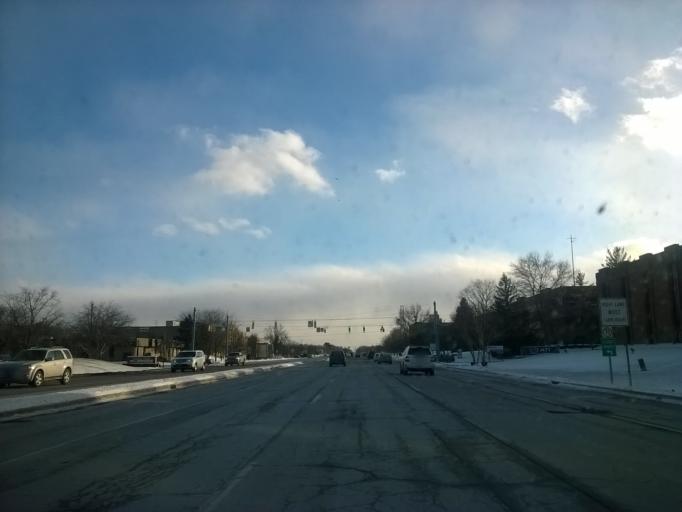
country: US
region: Indiana
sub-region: Marion County
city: Meridian Hills
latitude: 39.9242
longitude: -86.1580
